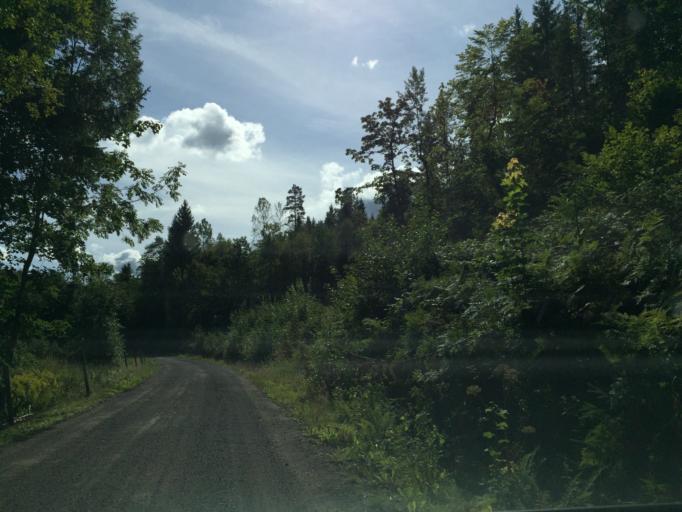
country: NO
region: Vestfold
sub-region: Hof
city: Hof
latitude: 59.4499
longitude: 10.1533
